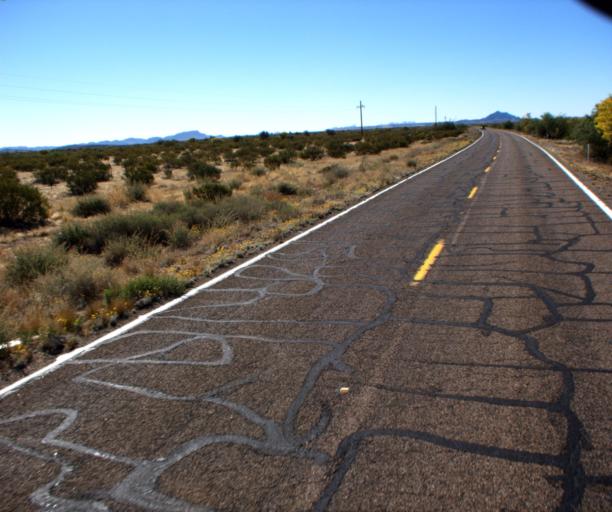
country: US
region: Arizona
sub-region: Pima County
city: Ajo
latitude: 32.4894
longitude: -112.8813
